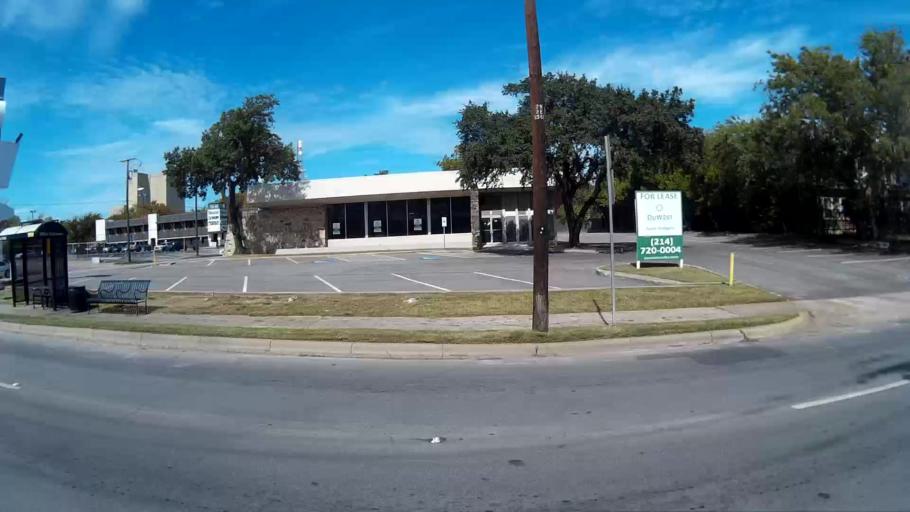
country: US
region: Texas
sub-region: Dallas County
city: Dallas
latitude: 32.7970
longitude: -96.7734
